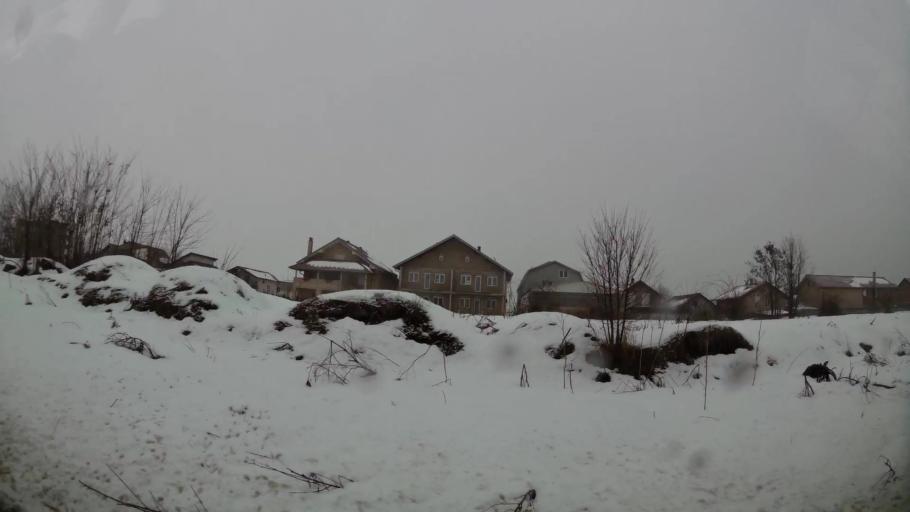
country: RS
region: Central Serbia
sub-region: Belgrade
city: Zemun
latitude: 44.8600
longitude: 20.3437
